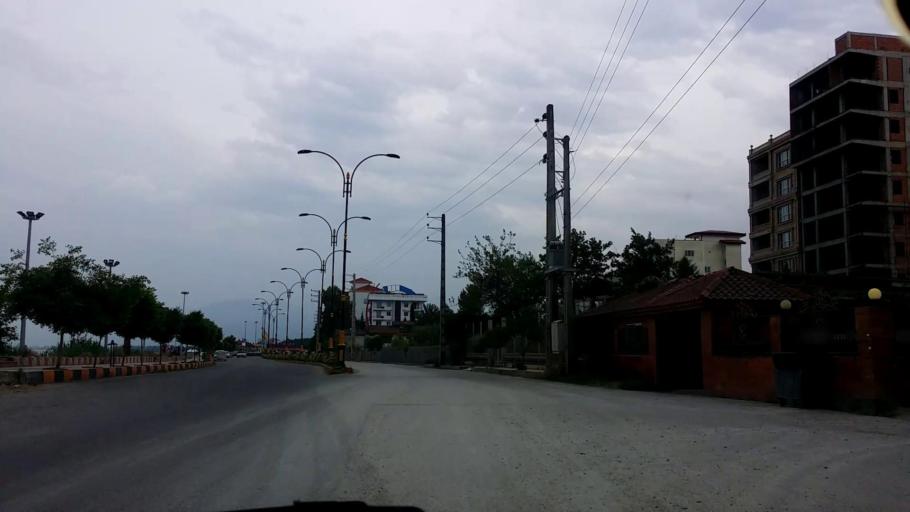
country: IR
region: Mazandaran
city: Chalus
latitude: 36.6824
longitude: 51.4345
